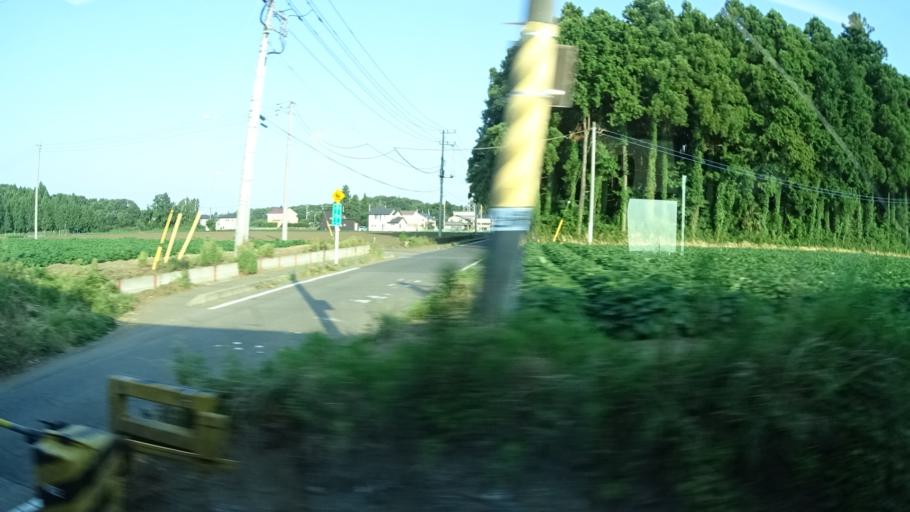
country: JP
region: Ibaraki
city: Funaishikawa
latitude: 36.4560
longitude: 140.5539
